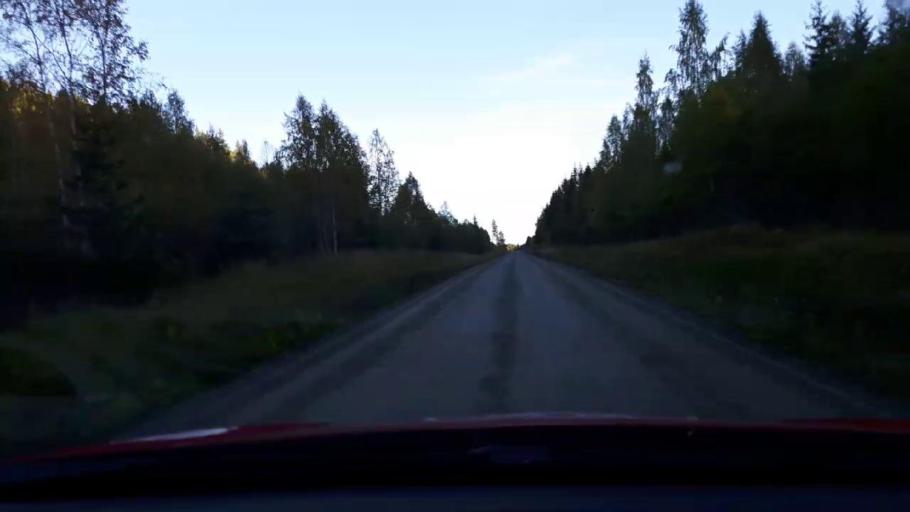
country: SE
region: Jaemtland
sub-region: OEstersunds Kommun
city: Brunflo
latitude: 62.9370
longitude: 14.9929
